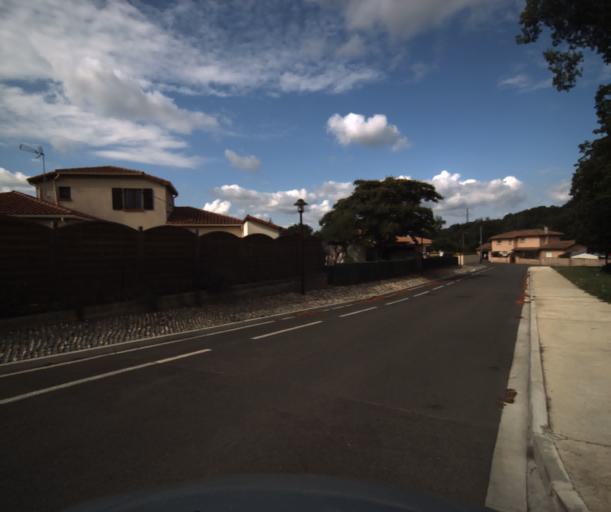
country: FR
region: Midi-Pyrenees
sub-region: Departement de la Haute-Garonne
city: Muret
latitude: 43.4450
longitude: 1.3241
